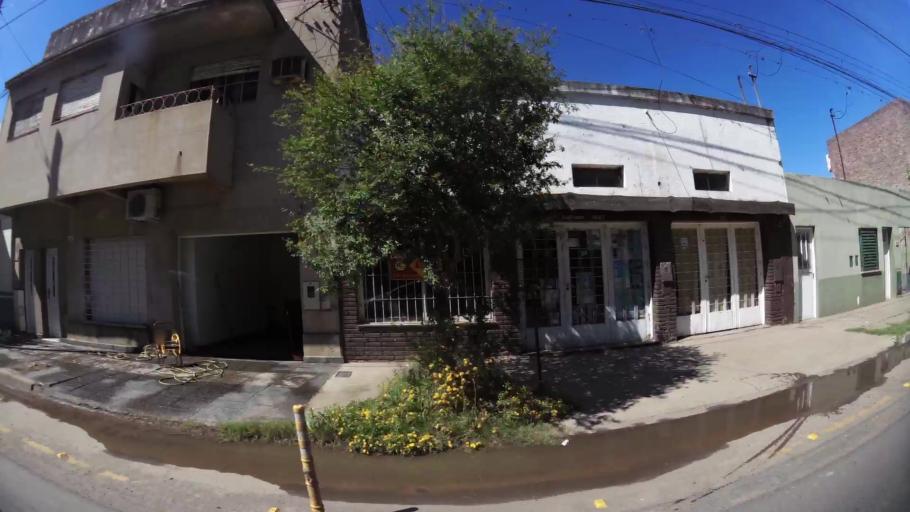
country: AR
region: Santa Fe
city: Esperanza
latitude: -31.4416
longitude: -60.9344
